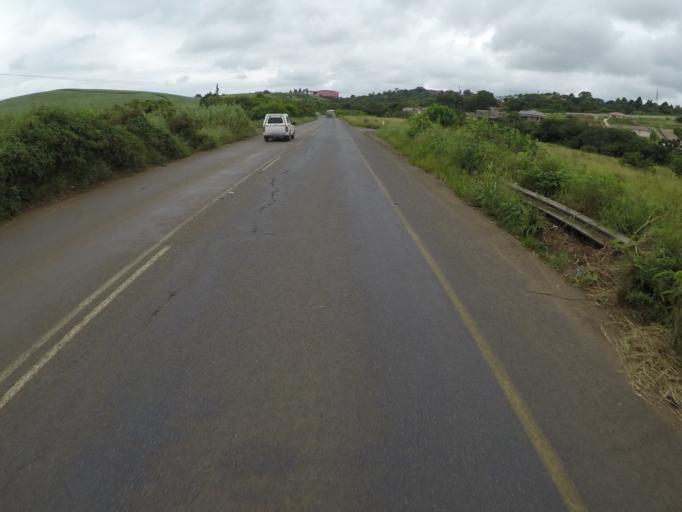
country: ZA
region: KwaZulu-Natal
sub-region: uThungulu District Municipality
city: Empangeni
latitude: -28.7506
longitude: 31.8784
